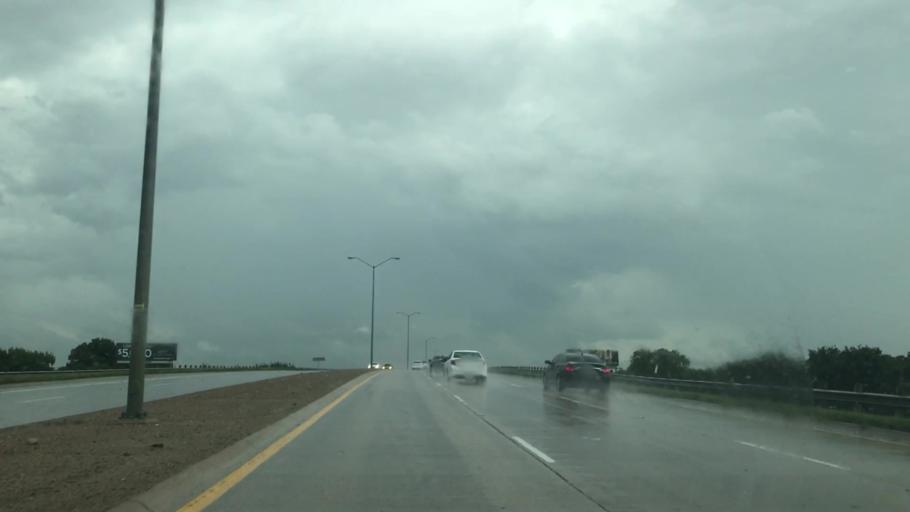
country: US
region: Texas
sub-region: Dallas County
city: Farmers Branch
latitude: 32.8707
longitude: -96.9191
